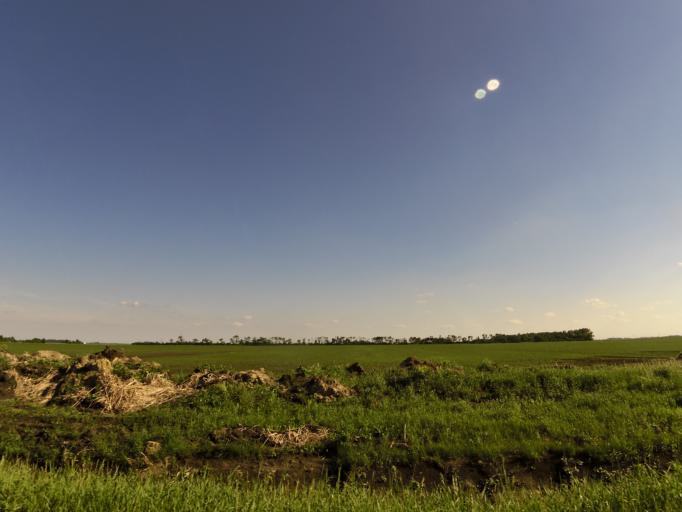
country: US
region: North Dakota
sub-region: Walsh County
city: Grafton
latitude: 48.3975
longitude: -97.2501
